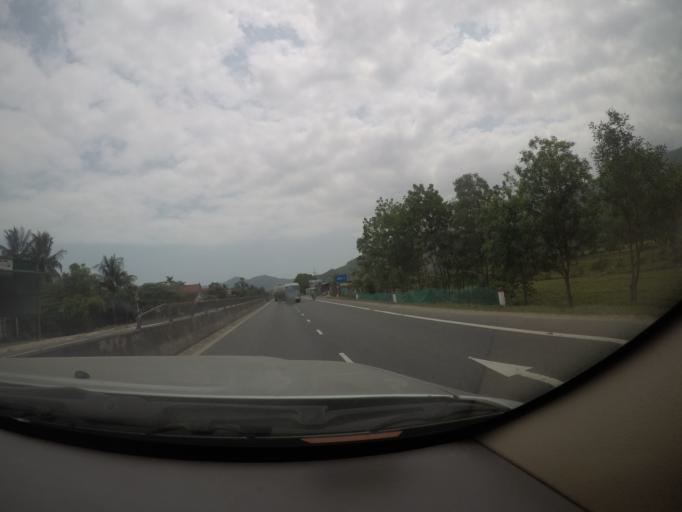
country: VN
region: Thua Thien-Hue
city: Phu Loc
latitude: 16.2711
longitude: 107.9980
